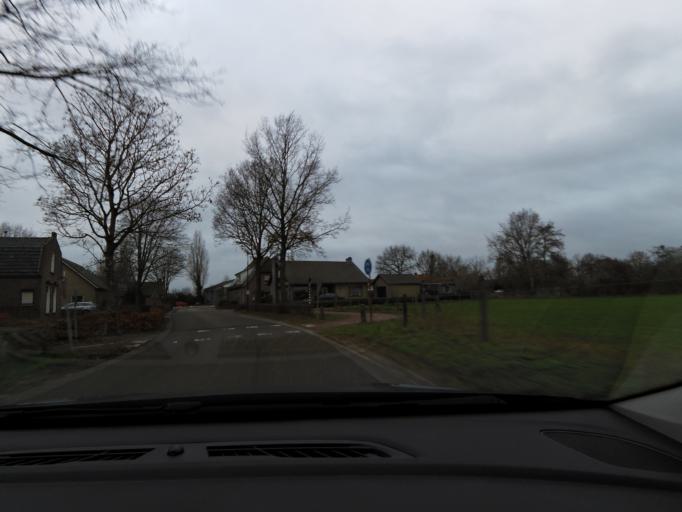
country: NL
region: North Brabant
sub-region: Gemeente Dongen
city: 's Gravenmoer
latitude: 51.6638
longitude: 4.9843
